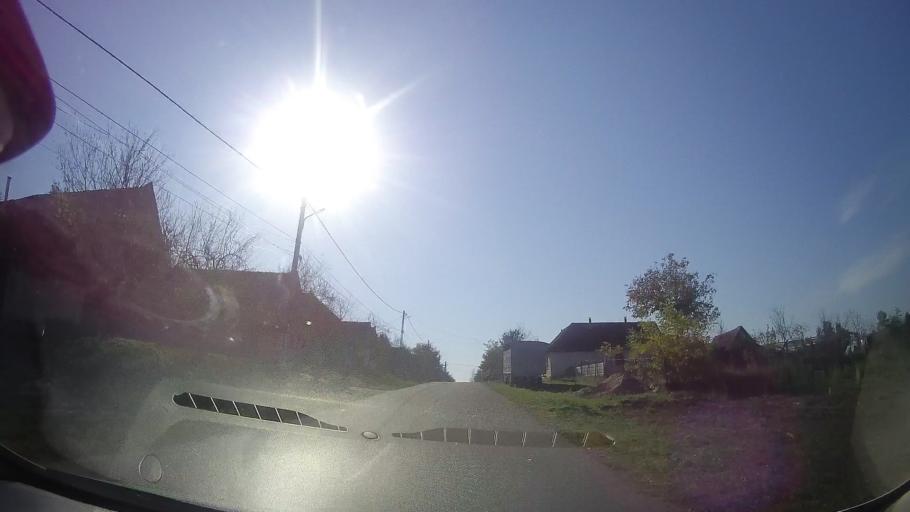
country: RO
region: Timis
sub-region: Comuna Topolovatu Mare
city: Topolovatu Mare
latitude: 45.8136
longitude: 21.5820
